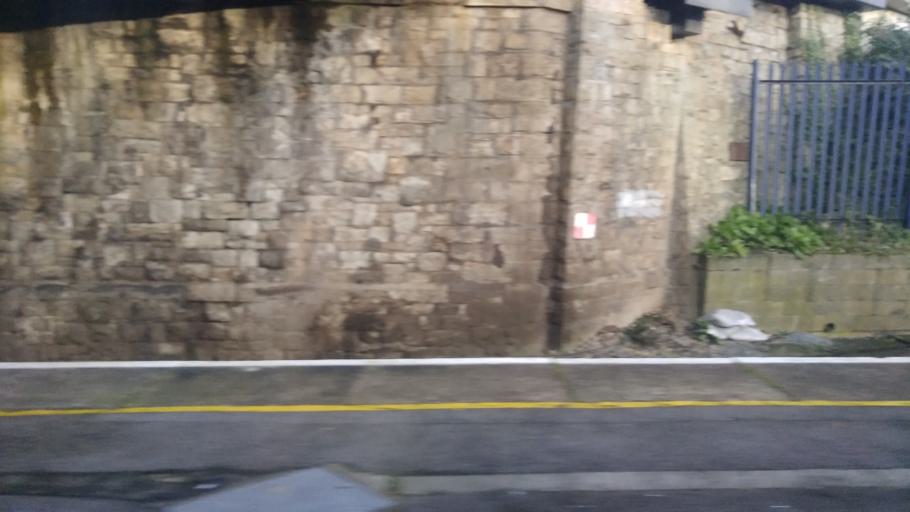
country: GB
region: England
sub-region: Kent
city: Sevenoaks
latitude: 51.2775
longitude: 0.1814
